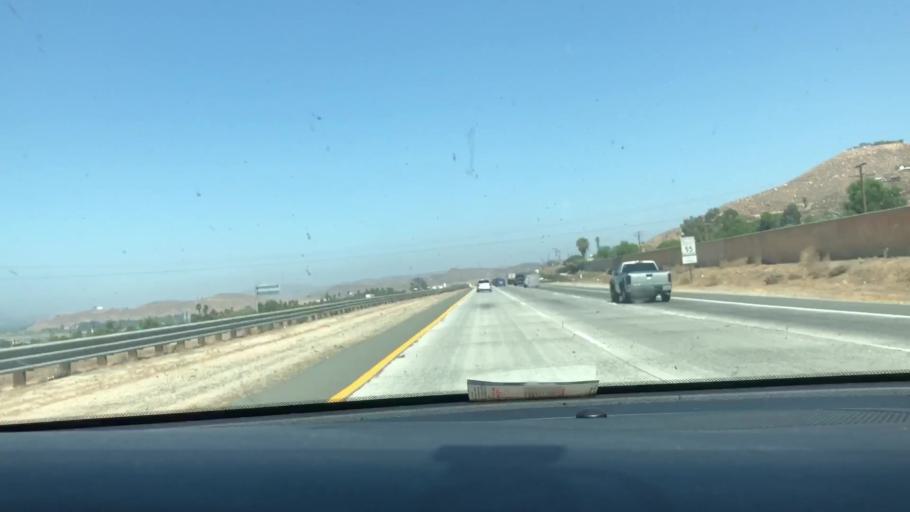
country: US
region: California
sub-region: Riverside County
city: Sedco Hills
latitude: 33.6403
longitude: -117.2823
